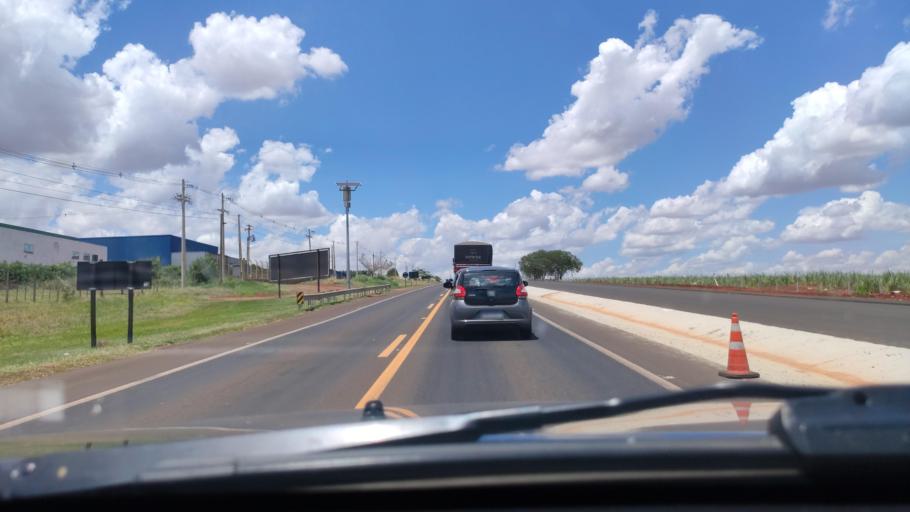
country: BR
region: Sao Paulo
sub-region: Jau
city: Jau
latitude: -22.2419
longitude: -48.5402
